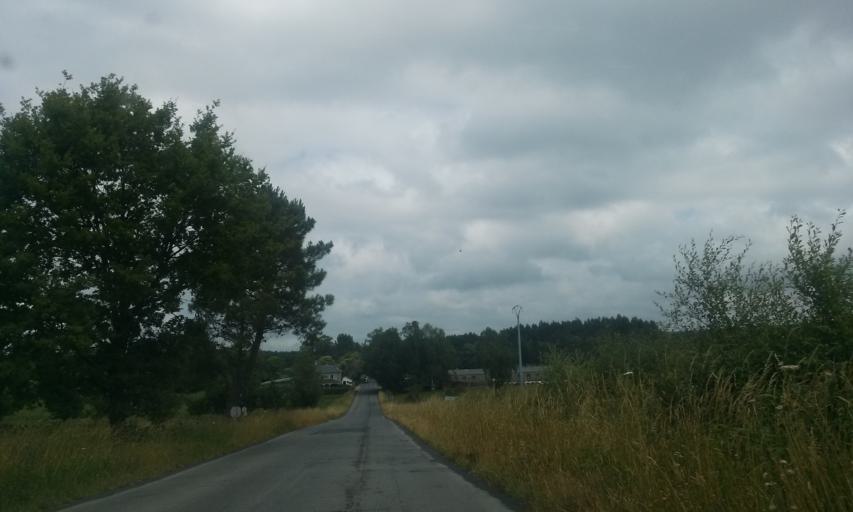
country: ES
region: Galicia
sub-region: Provincia de Lugo
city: Friol
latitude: 43.0898
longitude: -7.8096
